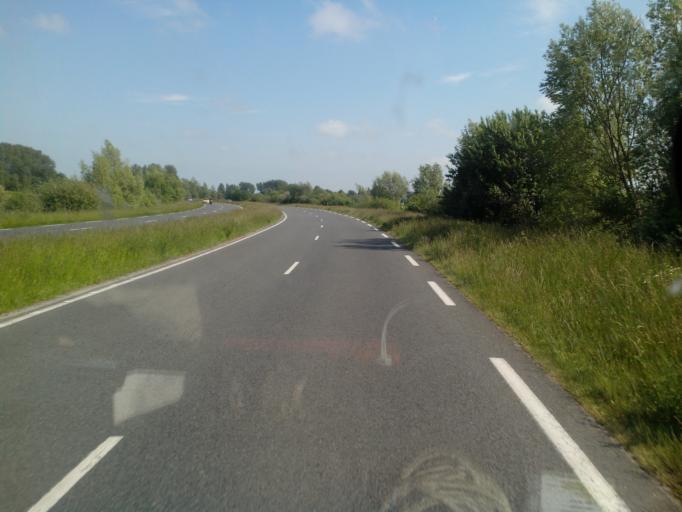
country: FR
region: Picardie
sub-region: Departement de la Somme
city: Rue
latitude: 50.2855
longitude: 1.6531
